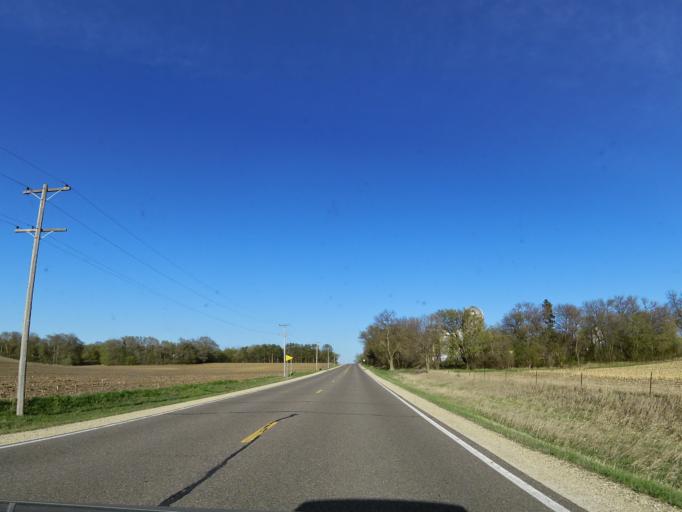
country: US
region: Minnesota
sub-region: Rice County
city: Northfield
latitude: 44.5436
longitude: -93.1138
